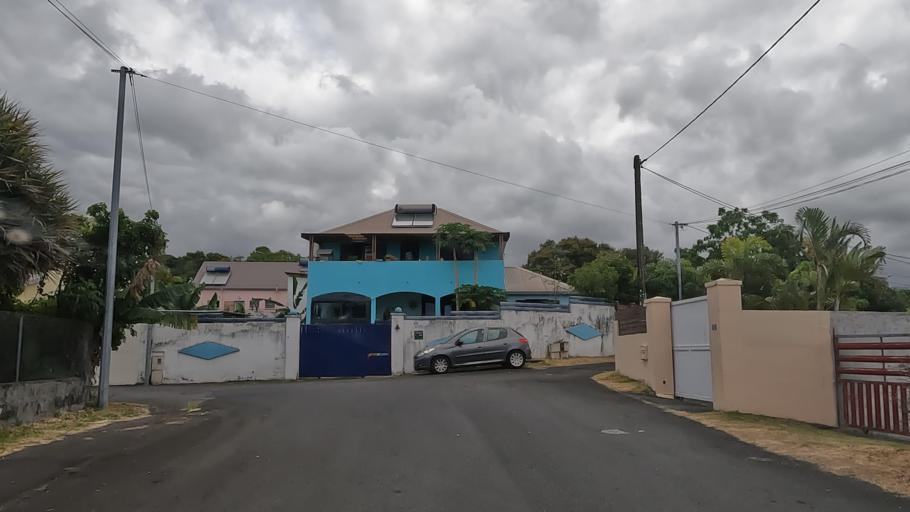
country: RE
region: Reunion
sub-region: Reunion
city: Saint-Benoit
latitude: -21.0895
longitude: 55.7458
